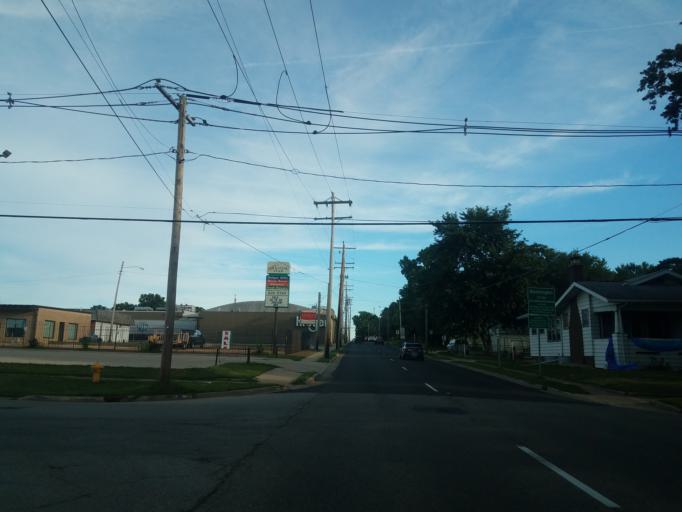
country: US
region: Illinois
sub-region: McLean County
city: Bloomington
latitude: 40.4953
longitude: -88.9953
